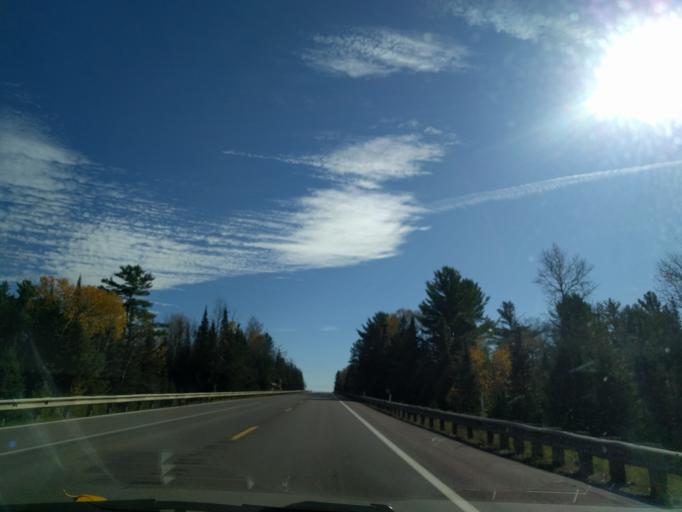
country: US
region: Michigan
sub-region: Marquette County
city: West Ishpeming
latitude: 46.3624
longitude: -87.9860
